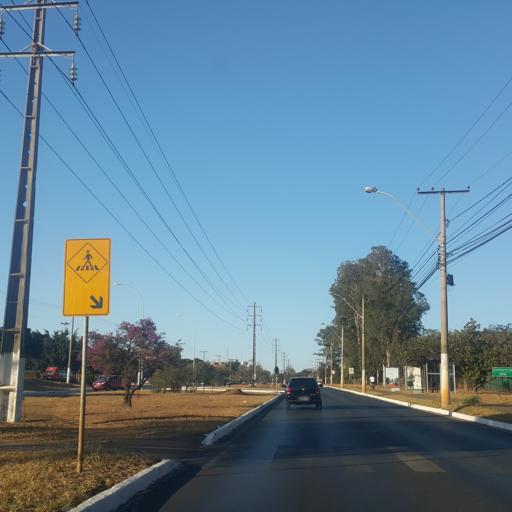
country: BR
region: Federal District
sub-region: Brasilia
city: Brasilia
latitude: -15.8017
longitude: -47.9391
